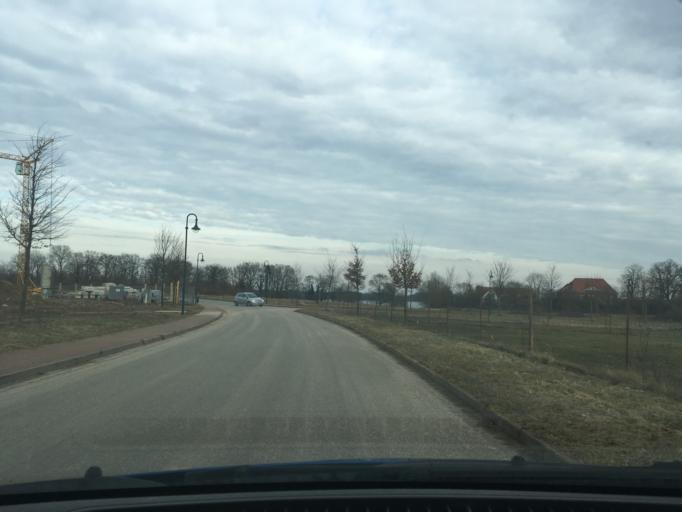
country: DE
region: Mecklenburg-Vorpommern
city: Zarrentin
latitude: 53.5568
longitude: 10.9144
